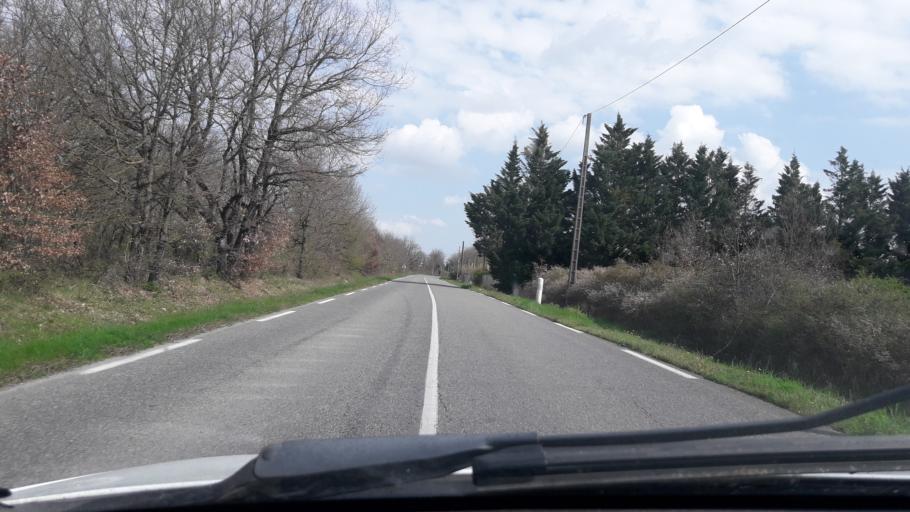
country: FR
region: Midi-Pyrenees
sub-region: Departement de la Haute-Garonne
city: Seysses
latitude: 43.5017
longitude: 1.2700
